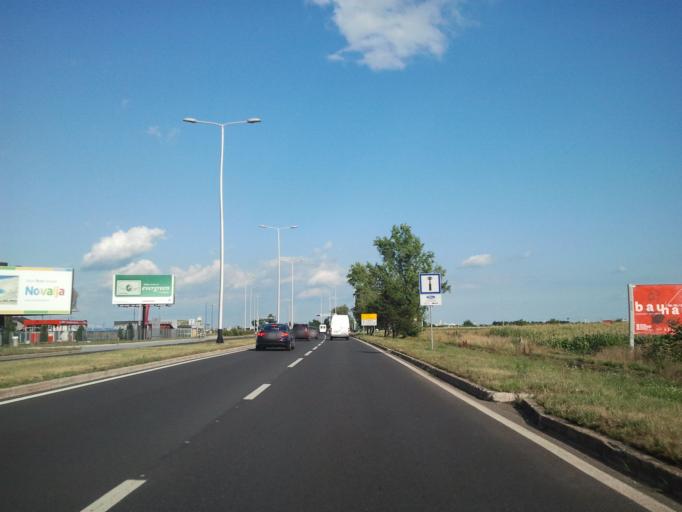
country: HR
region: Grad Zagreb
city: Odra
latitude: 45.7302
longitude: 16.0246
